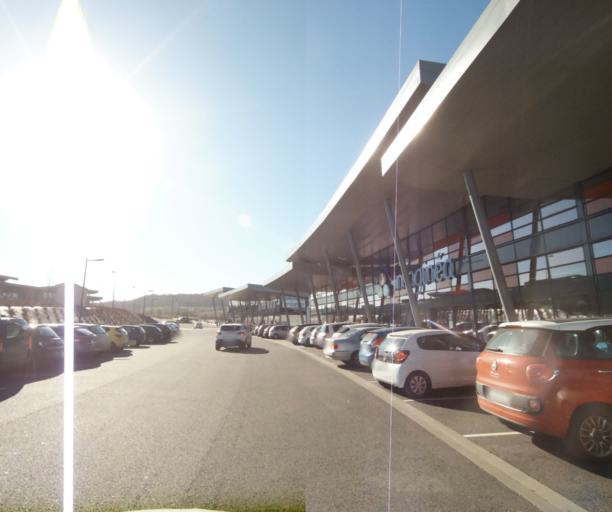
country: FR
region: Lorraine
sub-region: Departement de Meurthe-et-Moselle
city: Vandoeuvre-les-Nancy
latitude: 48.6396
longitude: 6.1898
